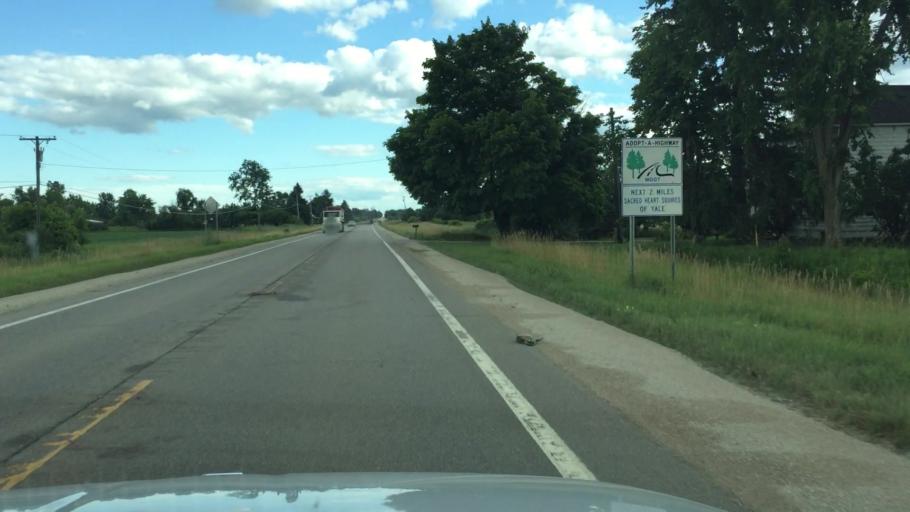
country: US
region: Michigan
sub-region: Saint Clair County
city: Yale
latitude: 43.1577
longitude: -82.8005
